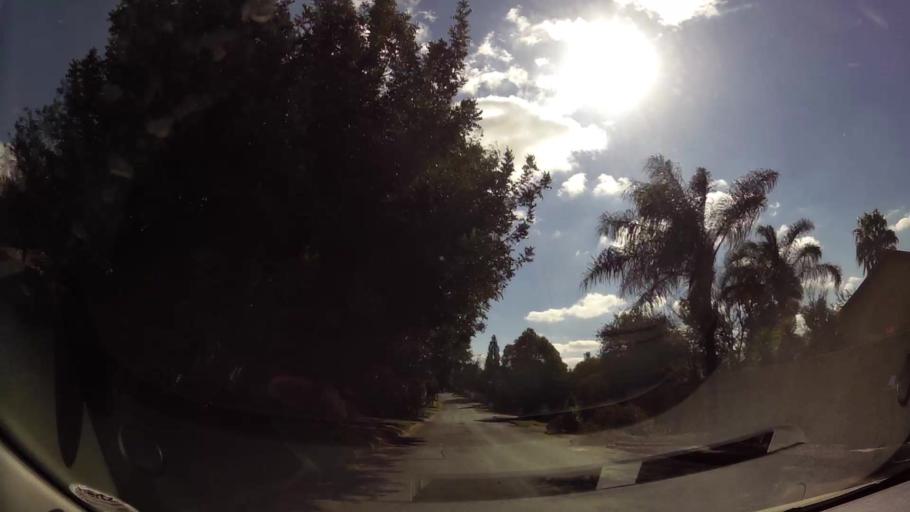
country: ZA
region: Gauteng
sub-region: West Rand District Municipality
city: Krugersdorp
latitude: -26.0868
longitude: 27.7951
